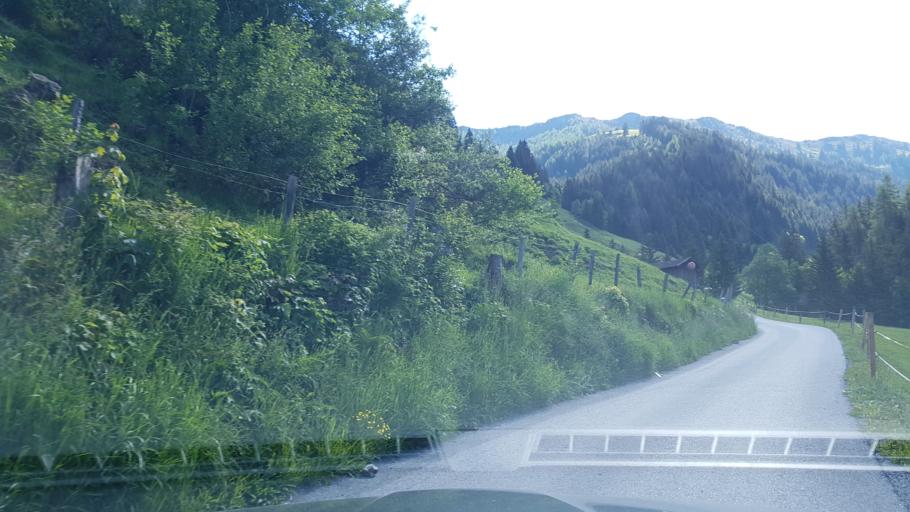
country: AT
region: Salzburg
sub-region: Politischer Bezirk Sankt Johann im Pongau
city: Kleinarl
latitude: 47.2361
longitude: 13.2618
